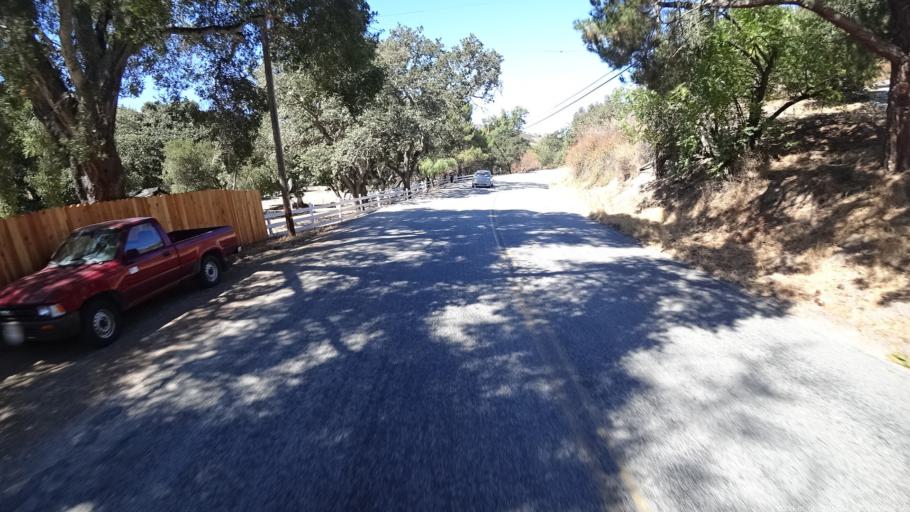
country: US
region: California
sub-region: Monterey County
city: Carmel Valley Village
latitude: 36.5512
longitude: -121.6900
